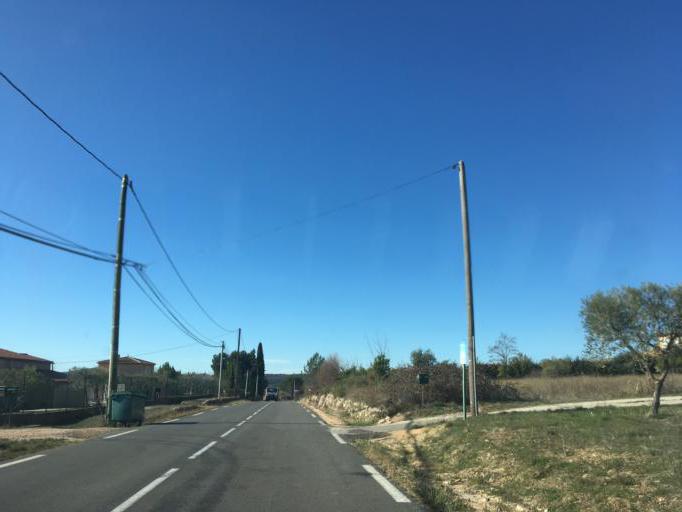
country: FR
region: Provence-Alpes-Cote d'Azur
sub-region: Departement du Var
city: Barjols
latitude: 43.5949
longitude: 6.0280
